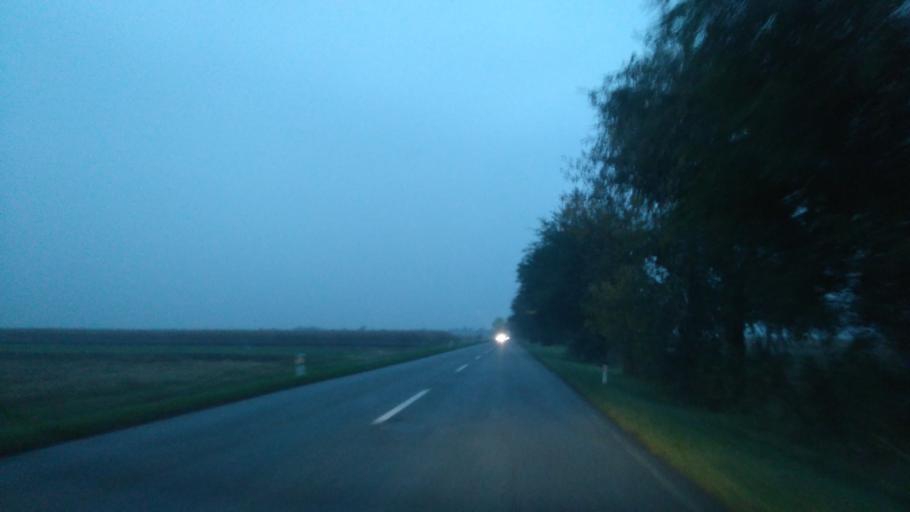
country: RS
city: Mol
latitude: 45.7398
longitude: 20.1167
